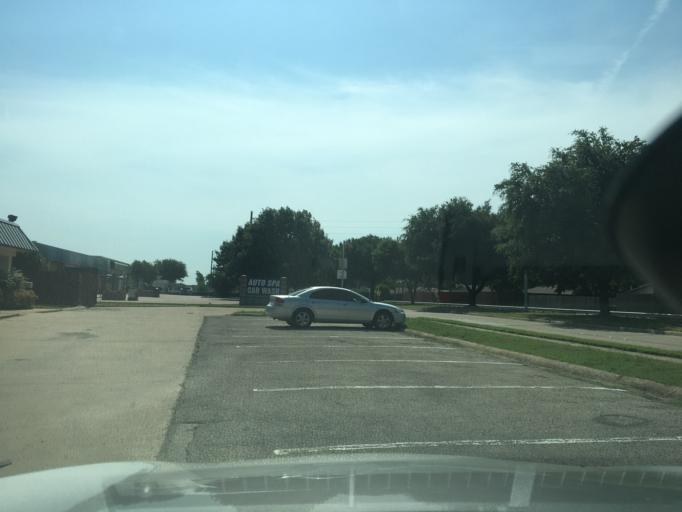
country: US
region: Texas
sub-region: Dallas County
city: Richardson
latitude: 32.9608
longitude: -96.6755
